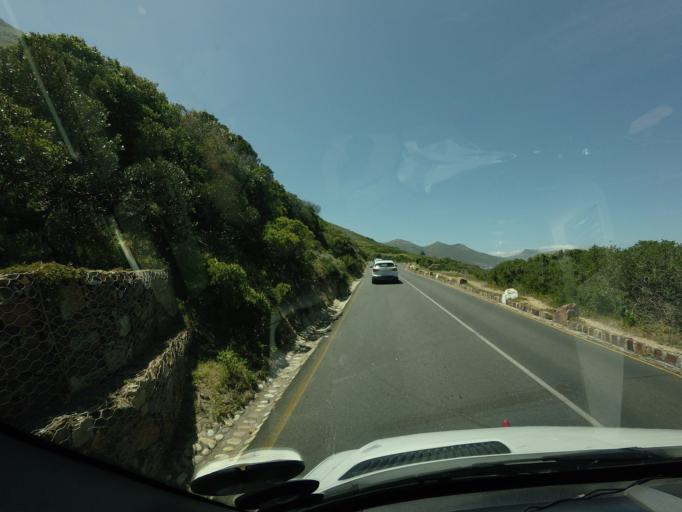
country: ZA
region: Western Cape
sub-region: City of Cape Town
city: Constantia
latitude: -34.0960
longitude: 18.3568
